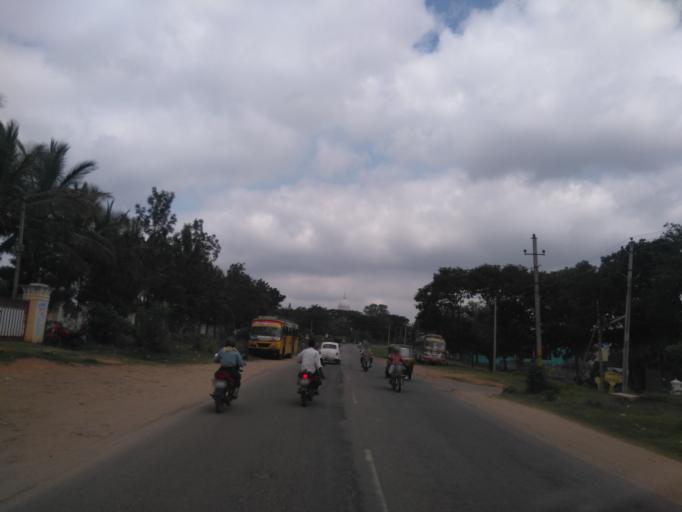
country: IN
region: Karnataka
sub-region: Mysore
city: Mysore
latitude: 12.2989
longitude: 76.6967
